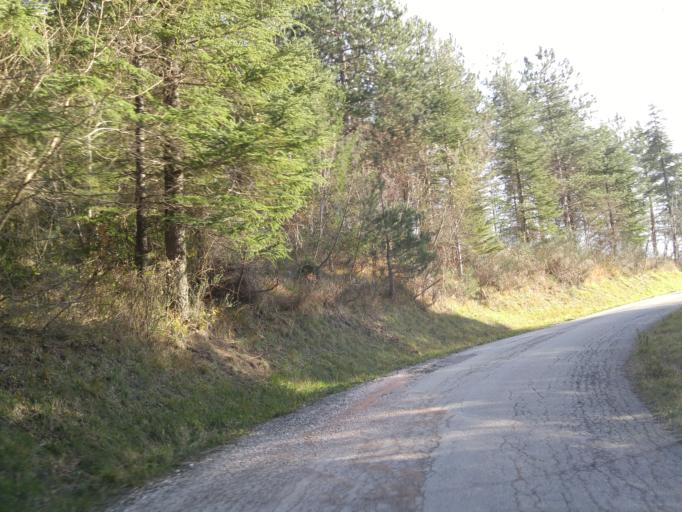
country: IT
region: The Marches
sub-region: Provincia di Pesaro e Urbino
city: Fermignano
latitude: 43.6778
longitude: 12.6765
